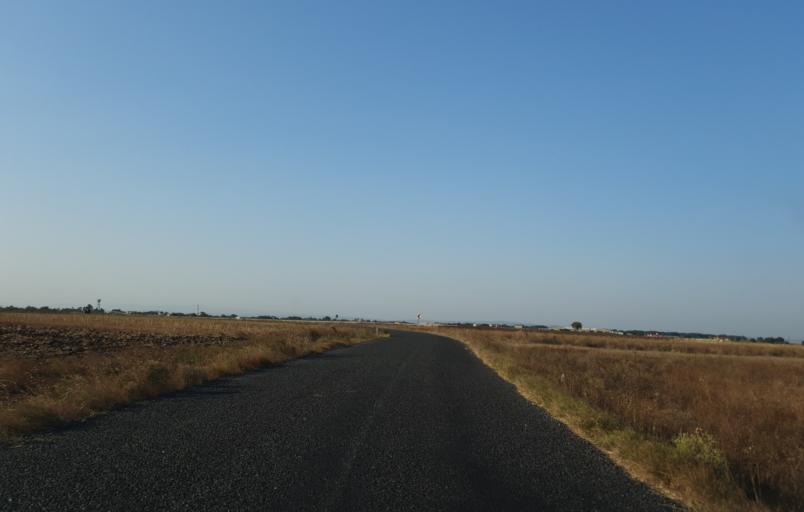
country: TR
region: Tekirdag
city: Beyazkoy
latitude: 41.4217
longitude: 27.7619
